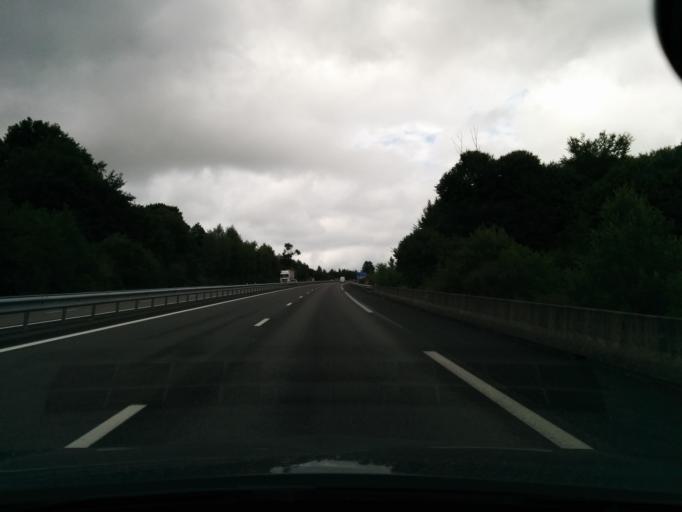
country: FR
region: Limousin
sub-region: Departement de la Correze
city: Vigeois
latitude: 45.3526
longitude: 1.5695
